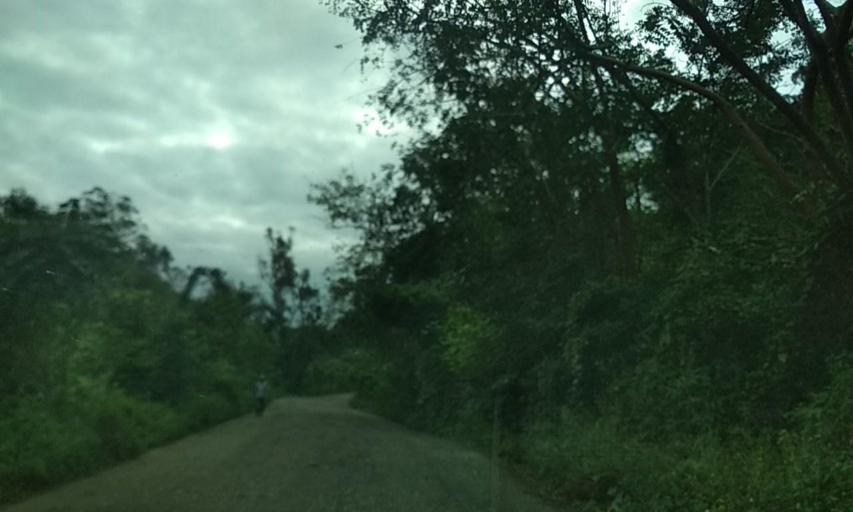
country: MX
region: Veracruz
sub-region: Papantla
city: Residencial Tajin
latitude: 20.6224
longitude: -97.3632
